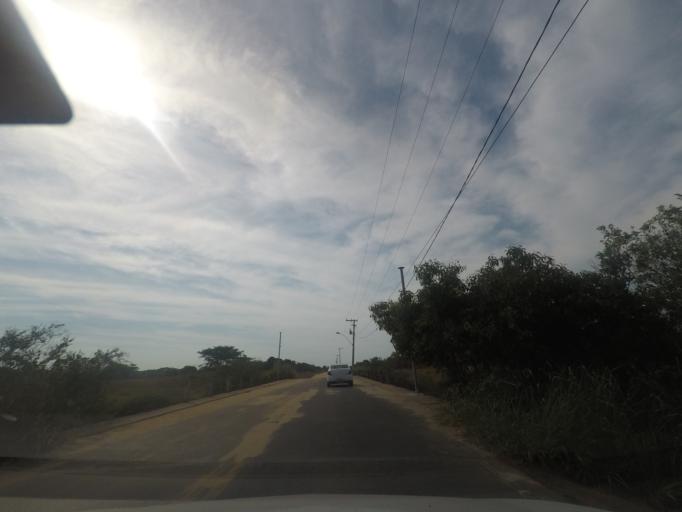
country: BR
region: Rio de Janeiro
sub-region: Marica
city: Marica
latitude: -22.9457
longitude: -42.8901
